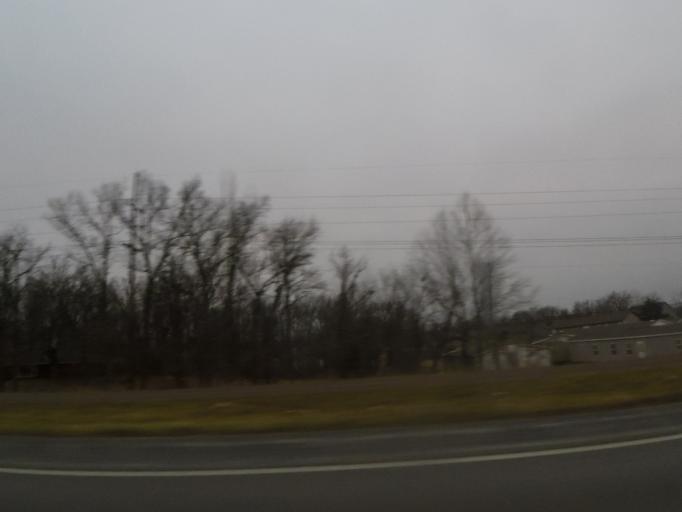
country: US
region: Missouri
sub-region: Lincoln County
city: Moscow Mills
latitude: 38.9617
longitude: -90.9499
